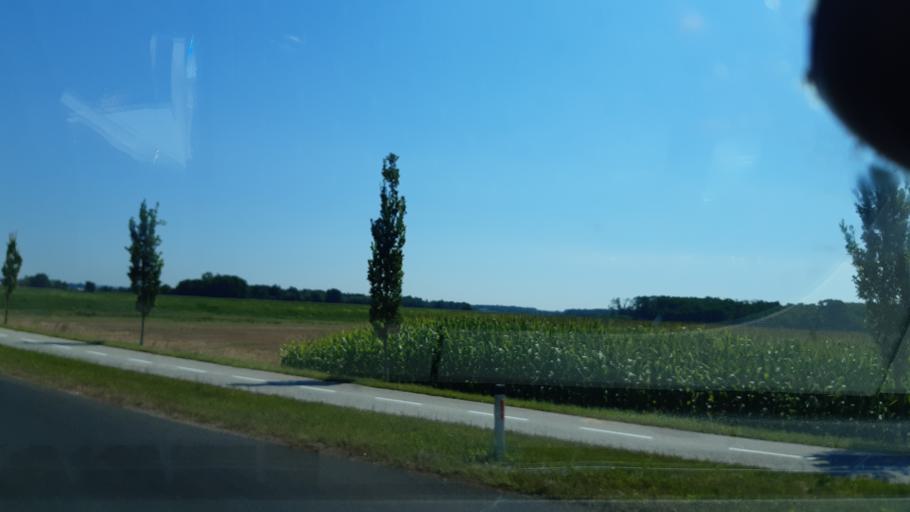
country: SI
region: Murska Sobota
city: Bakovci
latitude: 46.6298
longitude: 16.1558
